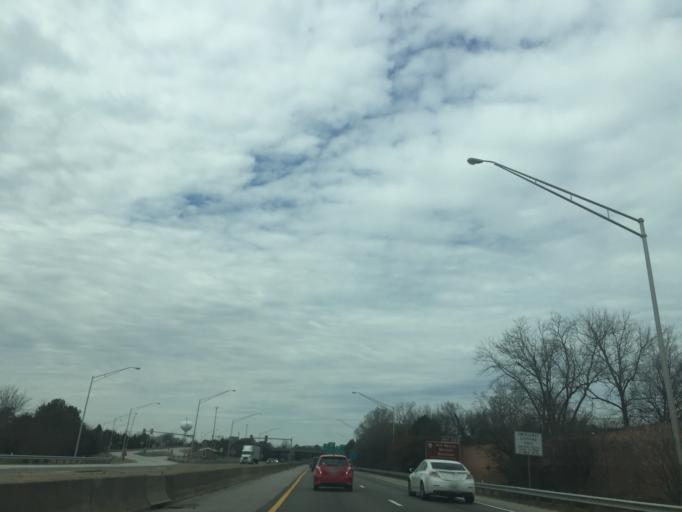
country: US
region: Virginia
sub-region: City of Hampton
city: East Hampton
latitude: 37.0134
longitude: -76.3243
